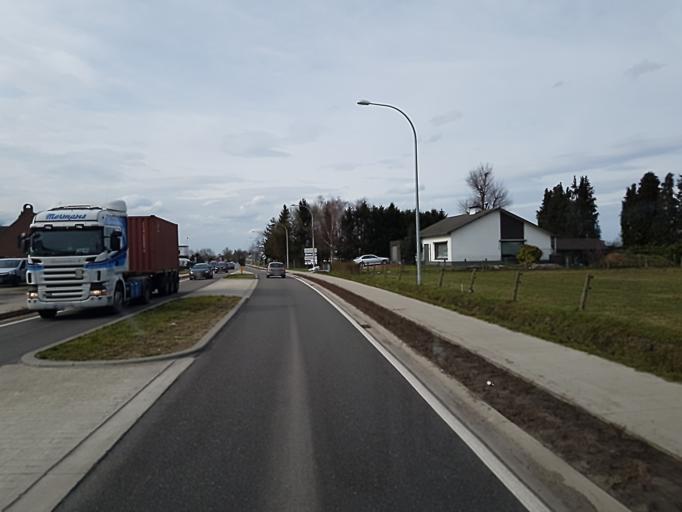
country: BE
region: Flanders
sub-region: Provincie Antwerpen
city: Dessel
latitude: 51.2532
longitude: 5.1061
